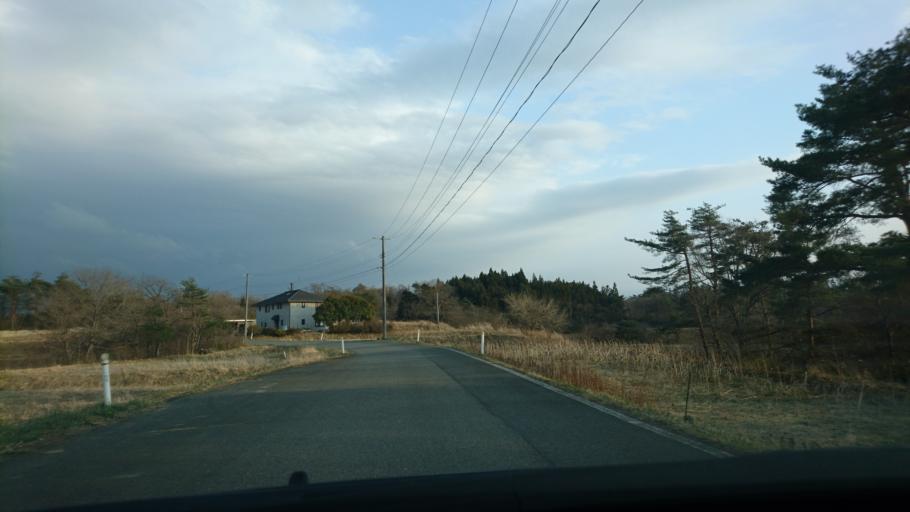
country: JP
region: Iwate
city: Ichinoseki
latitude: 38.8952
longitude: 141.2362
